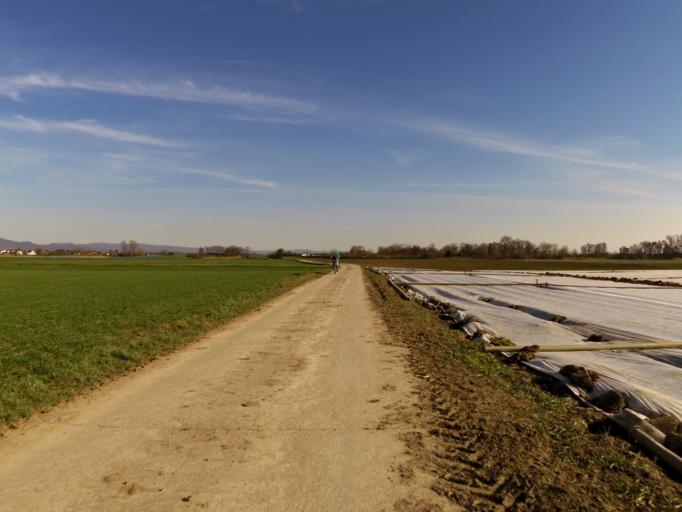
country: DE
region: Hesse
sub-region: Regierungsbezirk Darmstadt
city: Gross-Rohrheim
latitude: 49.7352
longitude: 8.4705
